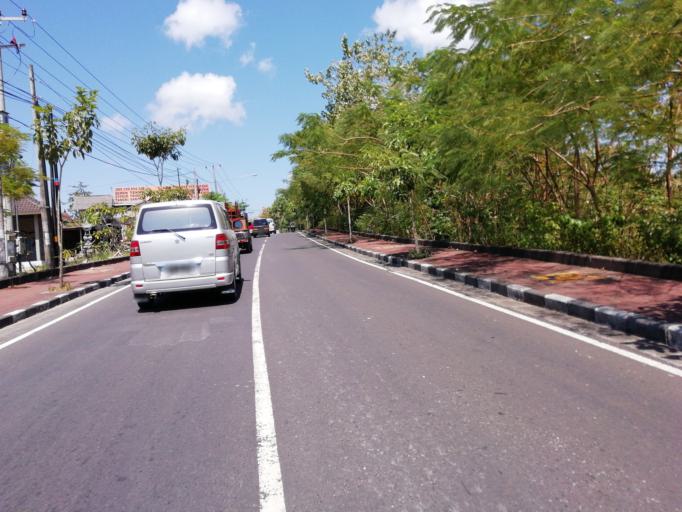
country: ID
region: Bali
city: Jimbaran
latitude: -8.7934
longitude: 115.1768
